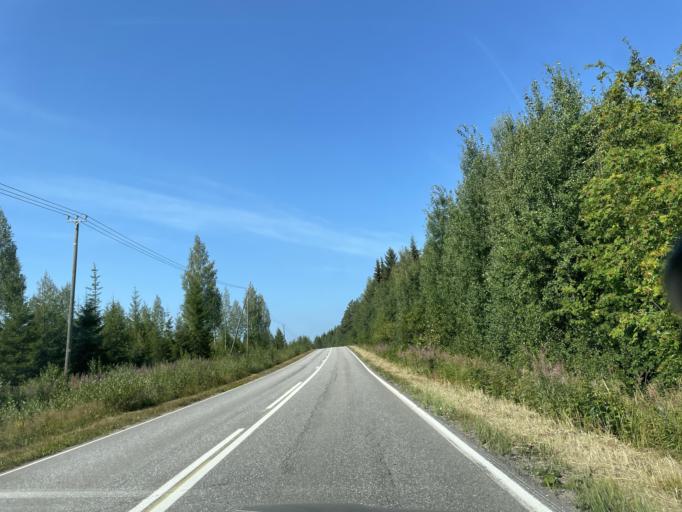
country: FI
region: Central Finland
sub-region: Saarijaervi-Viitasaari
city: Pihtipudas
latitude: 63.3536
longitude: 25.7758
